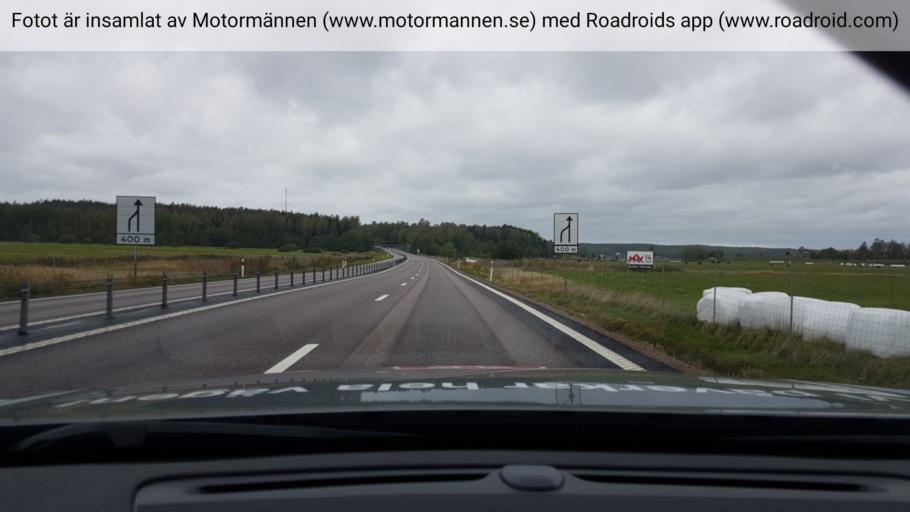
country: SE
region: Vaermland
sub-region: Karlstads Kommun
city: Skattkarr
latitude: 59.4137
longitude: 13.7492
